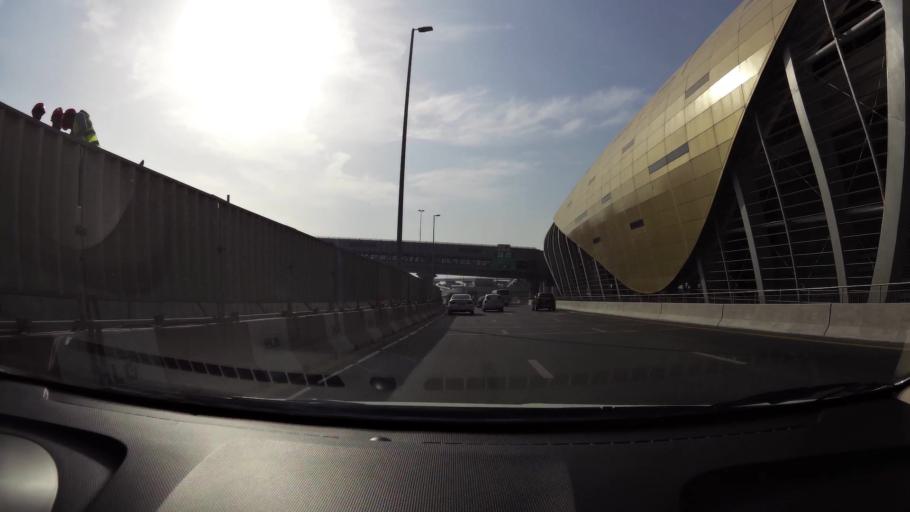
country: AE
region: Ash Shariqah
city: Sharjah
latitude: 25.2306
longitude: 55.3910
